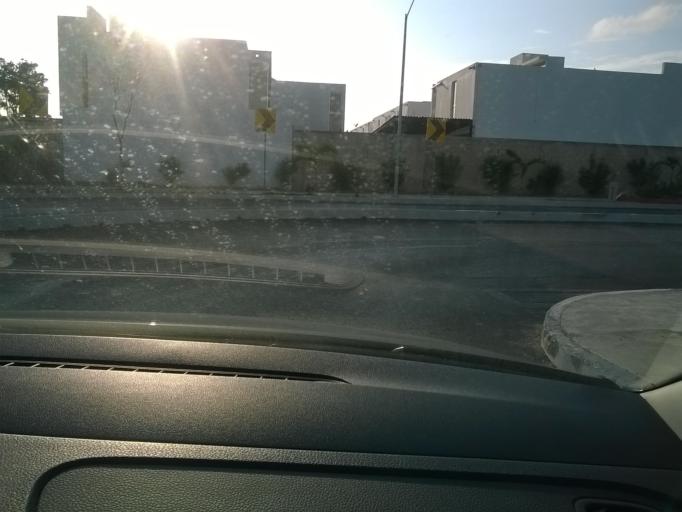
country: MX
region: Yucatan
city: Merida
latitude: 21.0380
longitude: -89.6343
